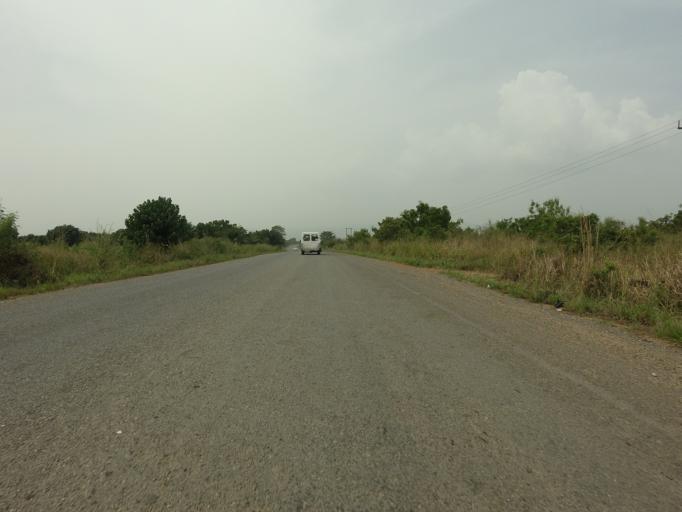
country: GH
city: Akropong
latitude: 6.0993
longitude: 0.0221
